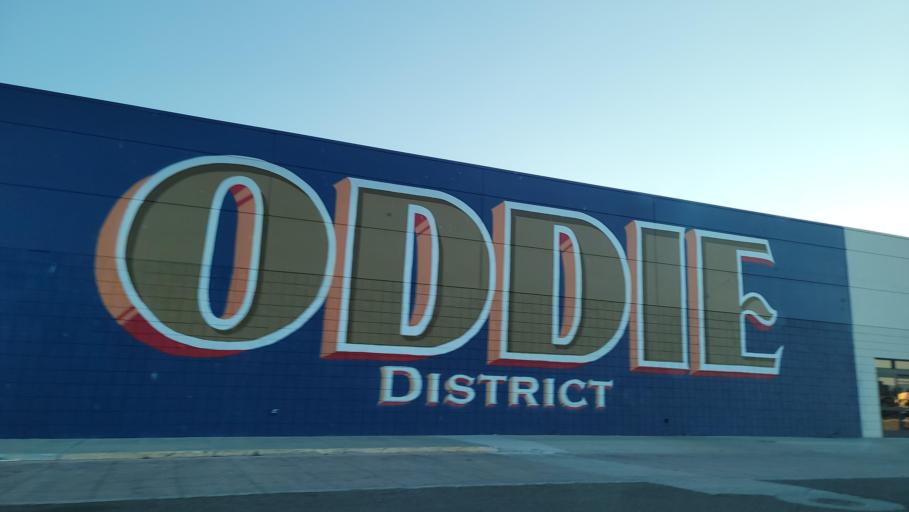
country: US
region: Nevada
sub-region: Washoe County
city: Sparks
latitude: 39.5469
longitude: -119.7800
